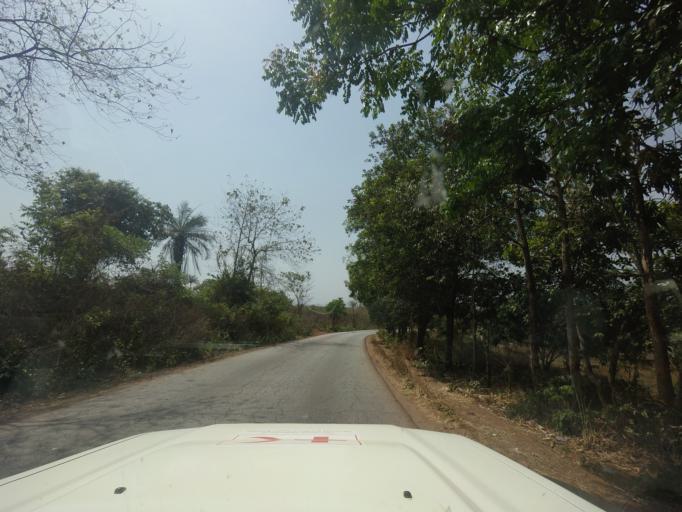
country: GN
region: Kindia
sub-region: Kindia
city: Kindia
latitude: 9.9704
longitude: -12.9351
